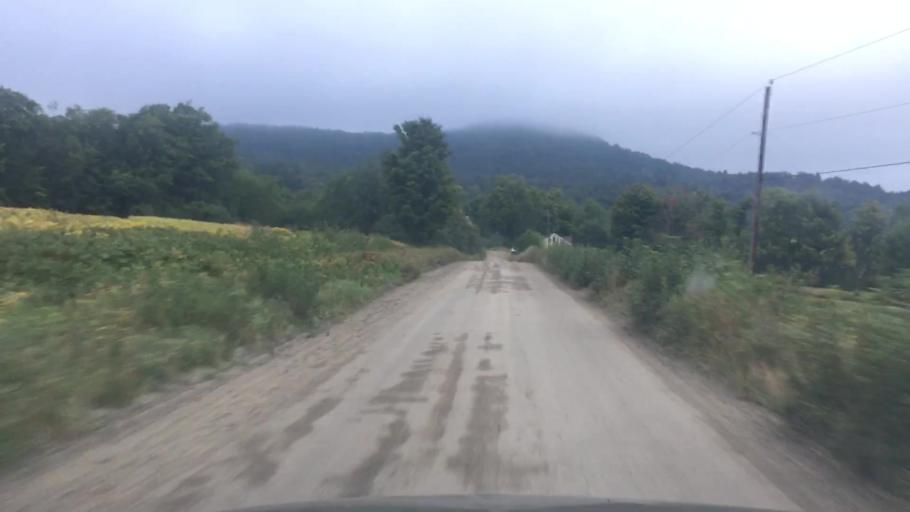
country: US
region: Vermont
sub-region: Windham County
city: Dover
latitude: 42.8553
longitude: -72.7790
